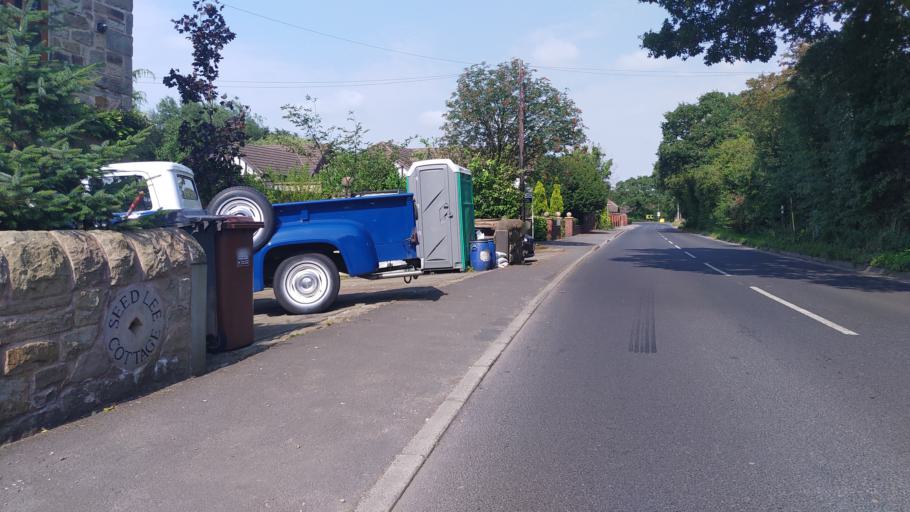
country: GB
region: England
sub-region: Lancashire
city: Clayton-le-Woods
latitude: 53.7211
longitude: -2.6367
